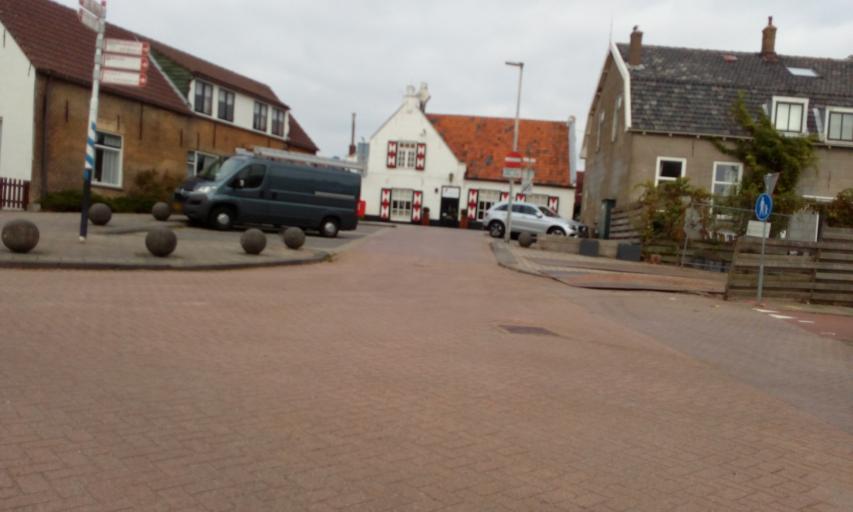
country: NL
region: South Holland
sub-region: Gemeente Albrandswaard
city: Rhoon
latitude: 51.8494
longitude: 4.4211
